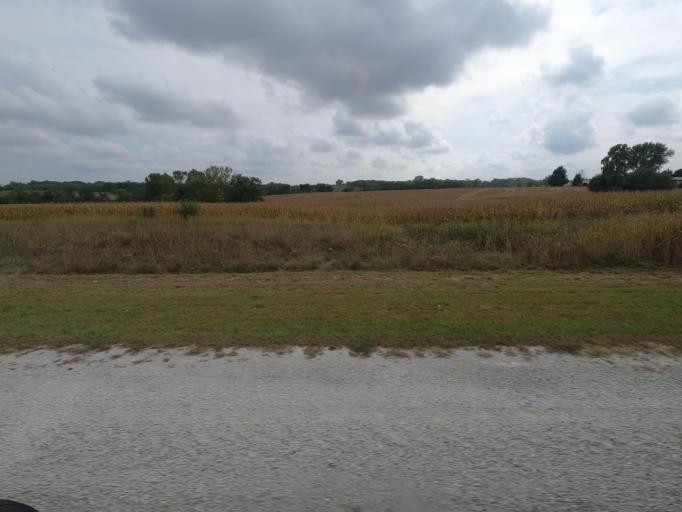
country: US
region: Iowa
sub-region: Wapello County
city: Ottumwa
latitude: 41.0037
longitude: -92.2884
